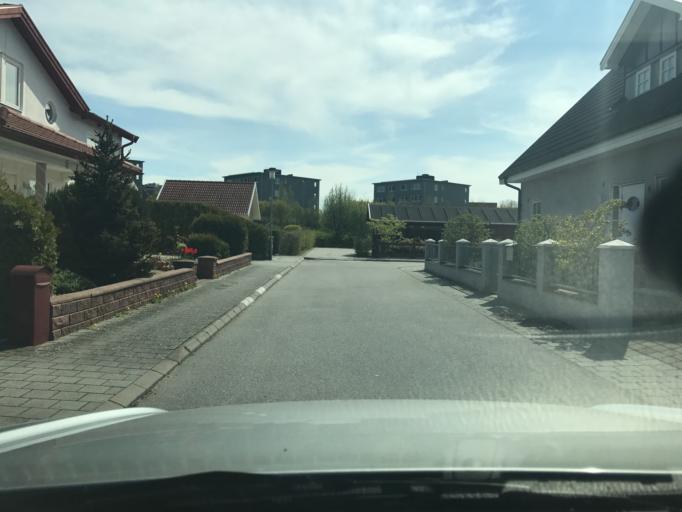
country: SE
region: Skane
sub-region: Burlovs Kommun
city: Arloev
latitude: 55.5964
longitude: 13.0929
